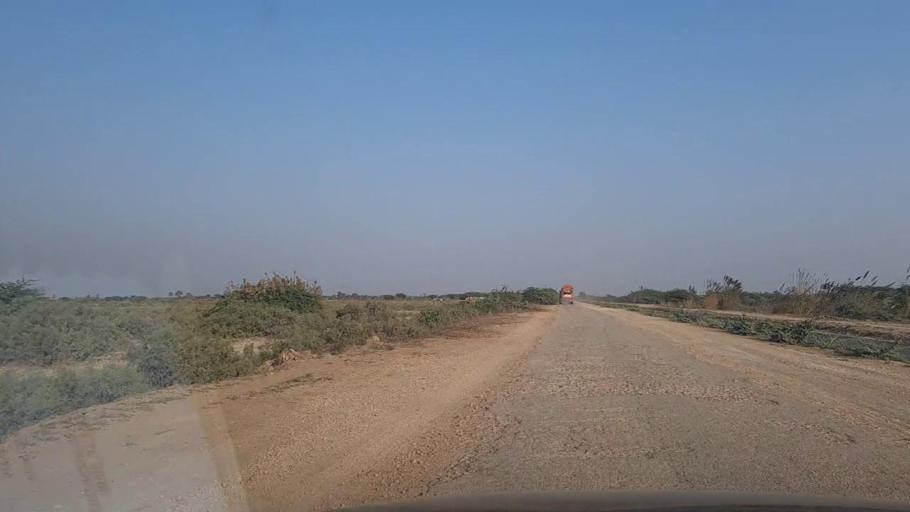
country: PK
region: Sindh
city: Keti Bandar
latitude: 24.2650
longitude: 67.5477
